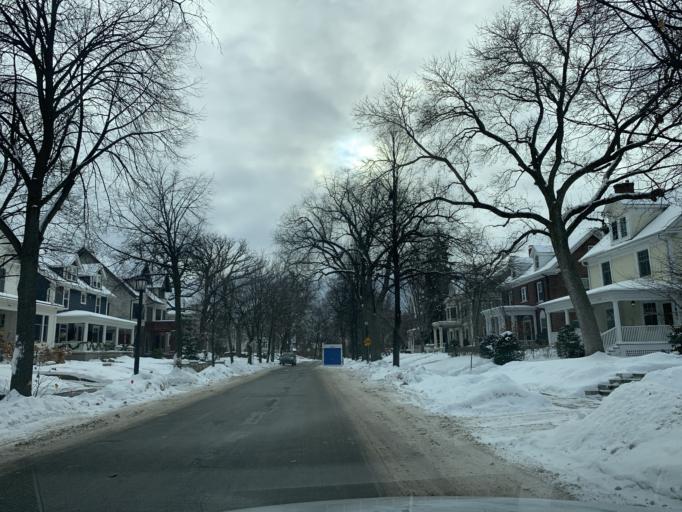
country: US
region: Minnesota
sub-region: Hennepin County
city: Minneapolis
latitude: 44.9640
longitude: -93.2995
